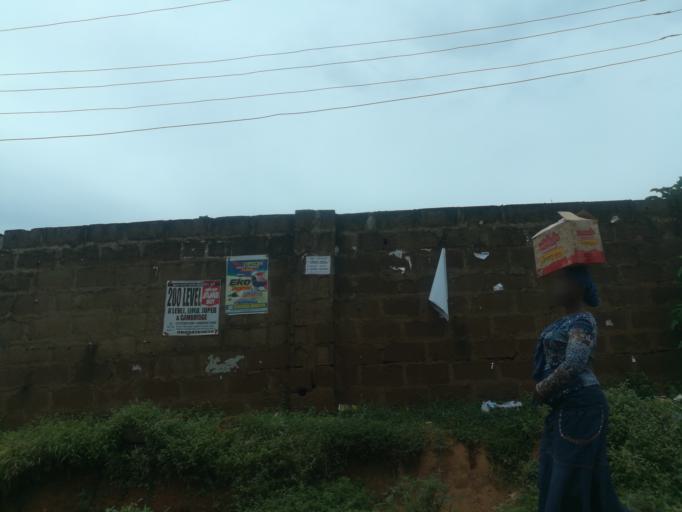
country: NG
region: Oyo
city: Ibadan
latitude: 7.3367
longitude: 3.9006
